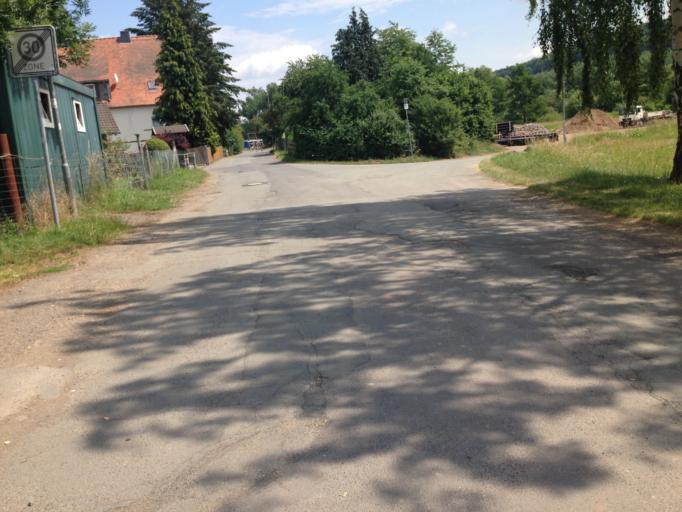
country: DE
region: Hesse
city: Wetter
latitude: 50.8602
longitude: 8.7079
